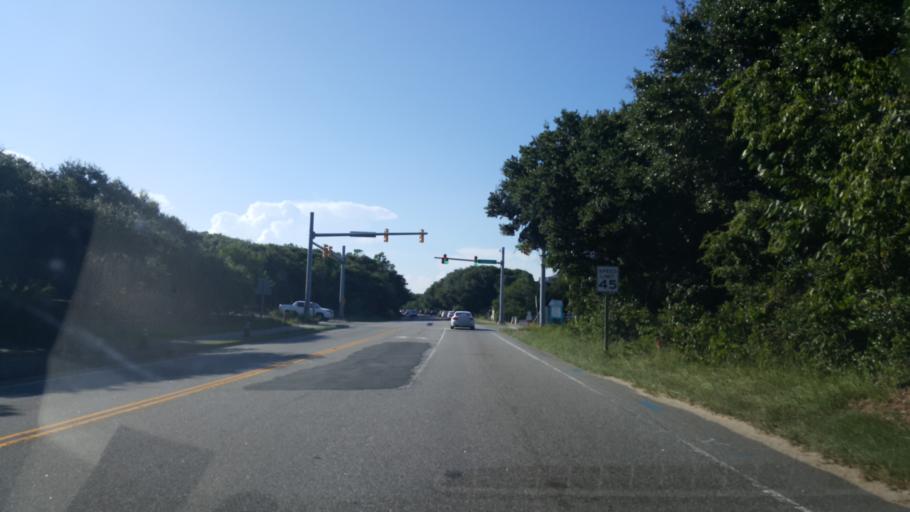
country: US
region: North Carolina
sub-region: Dare County
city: Southern Shores
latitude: 36.1284
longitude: -75.7294
